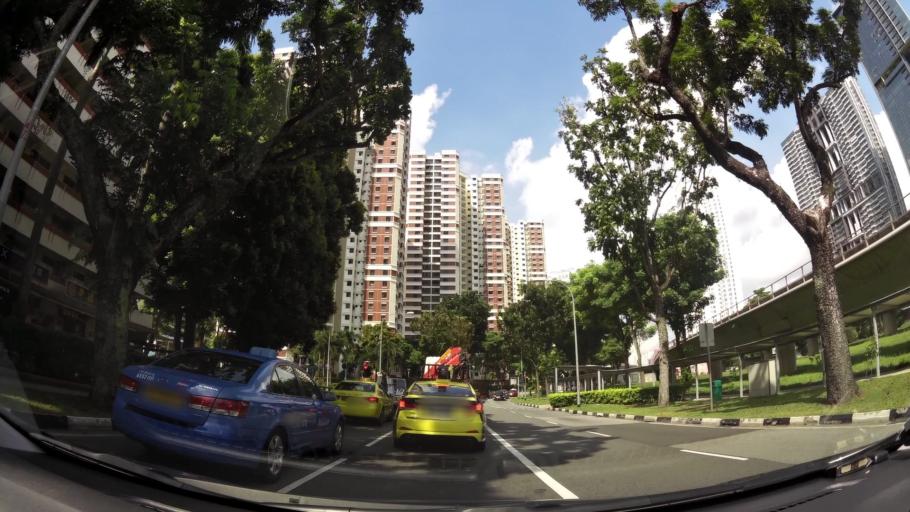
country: SG
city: Singapore
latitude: 1.2887
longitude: 103.8184
